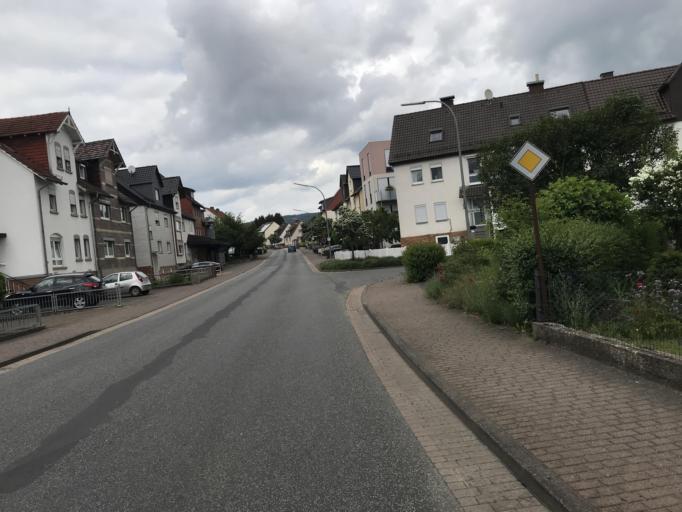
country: DE
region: Hesse
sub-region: Regierungsbezirk Kassel
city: Baunatal
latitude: 51.2511
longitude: 9.3832
